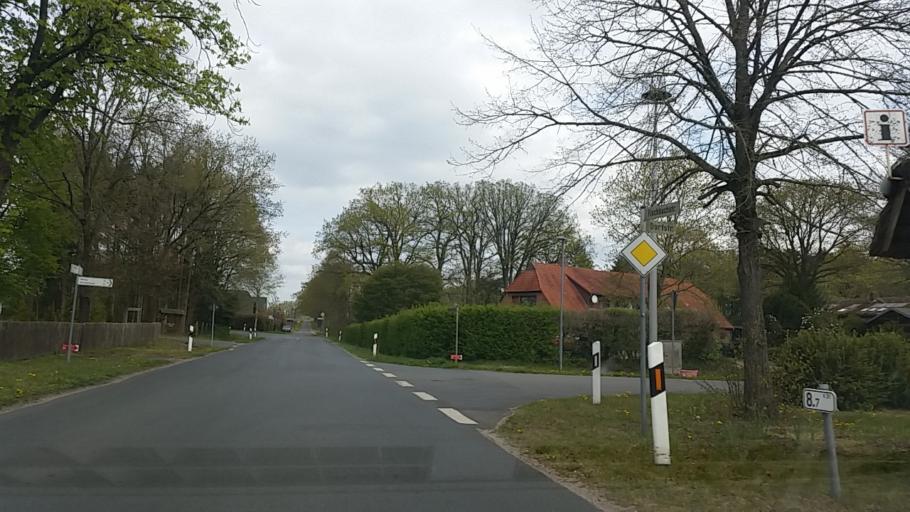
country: DE
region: Lower Saxony
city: Otter
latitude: 53.1874
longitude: 9.7411
